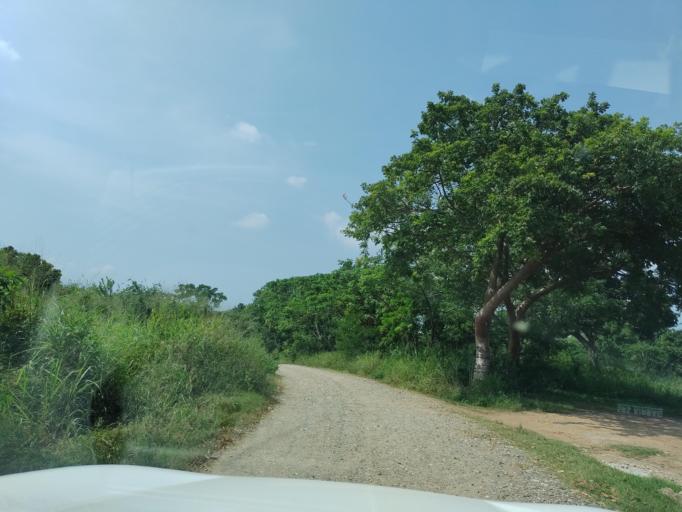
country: MX
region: Veracruz
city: Martinez de la Torre
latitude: 20.0904
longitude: -97.0491
